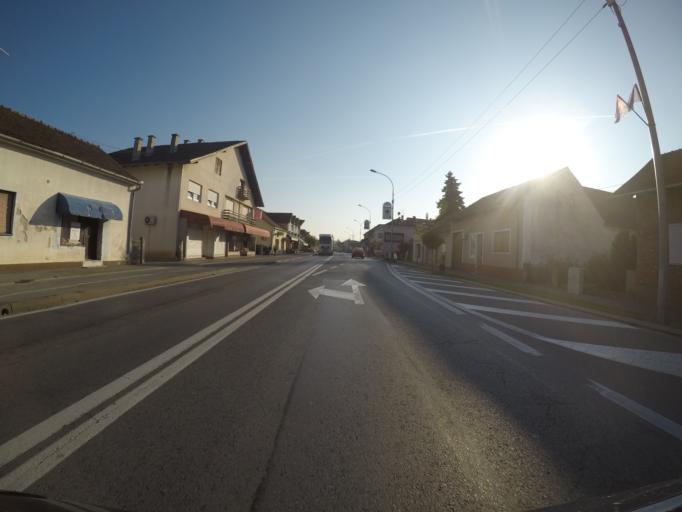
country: HR
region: Virovitick-Podravska
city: Pitomaca
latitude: 45.9508
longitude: 17.2328
